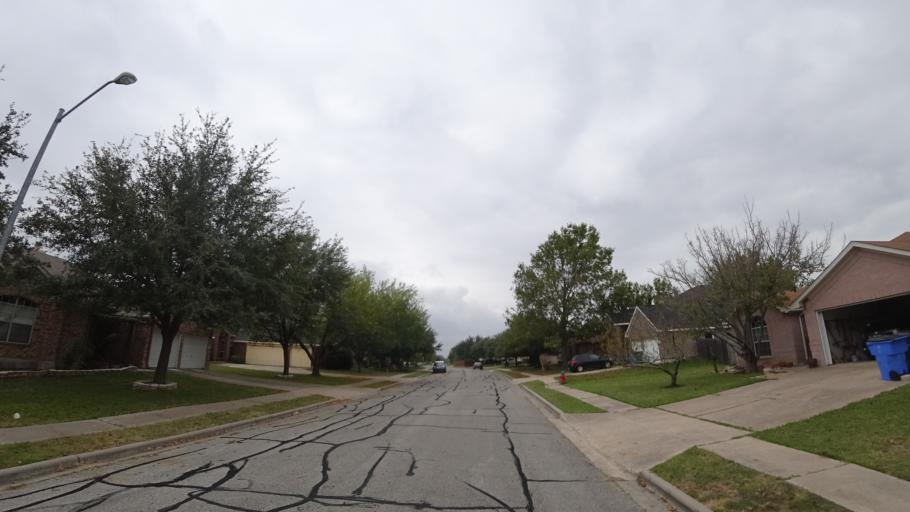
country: US
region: Texas
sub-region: Travis County
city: Pflugerville
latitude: 30.4351
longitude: -97.6209
